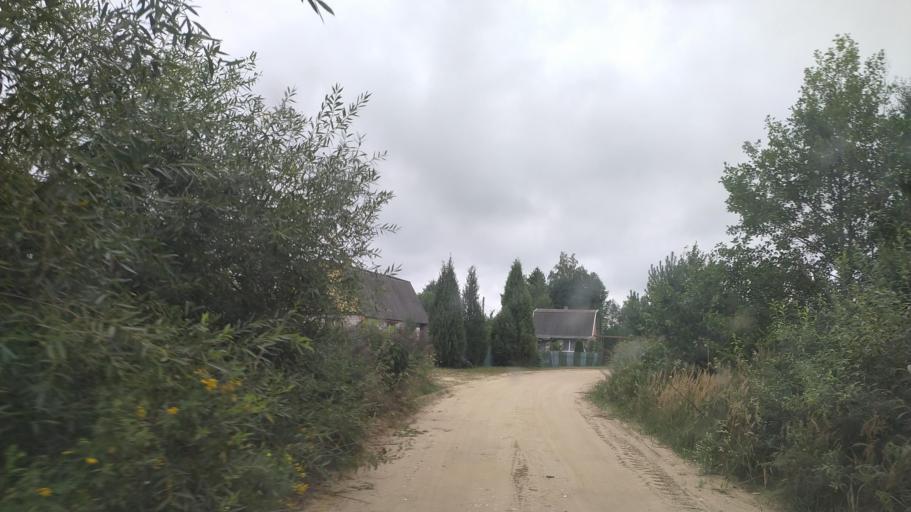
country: BY
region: Brest
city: Byaroza
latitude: 52.6015
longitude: 24.8830
